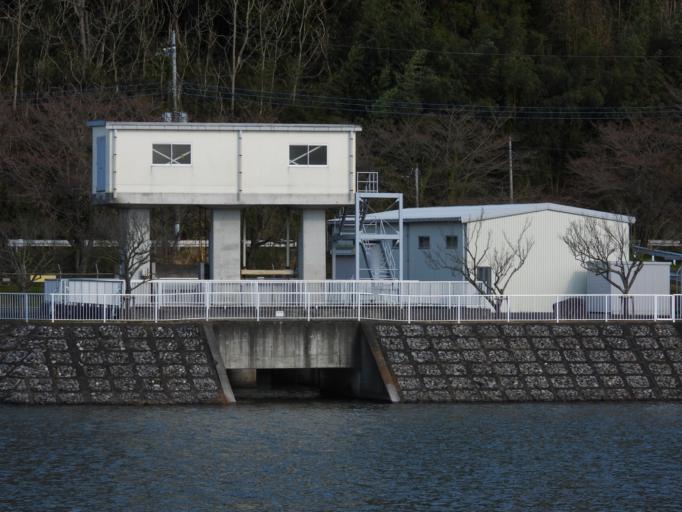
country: JP
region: Ibaraki
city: Makabe
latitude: 36.2381
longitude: 140.0695
